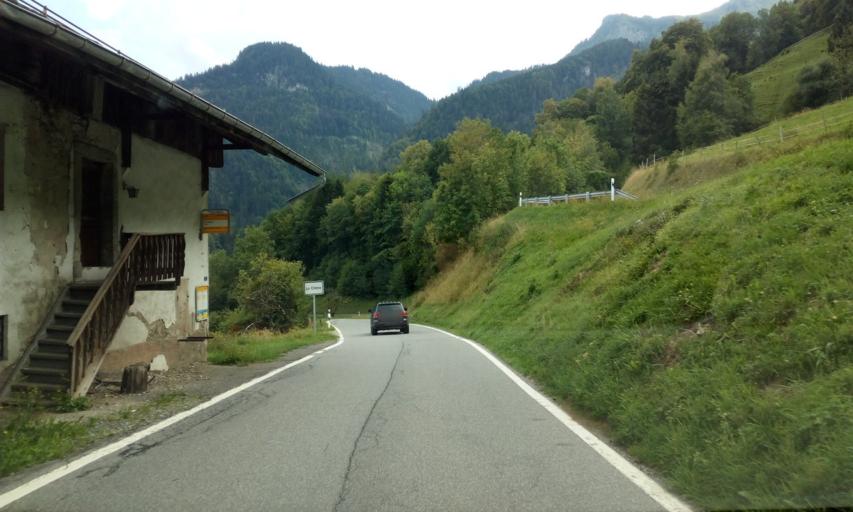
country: CH
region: Valais
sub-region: Monthey District
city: Vionnaz
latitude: 46.3093
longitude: 6.8873
